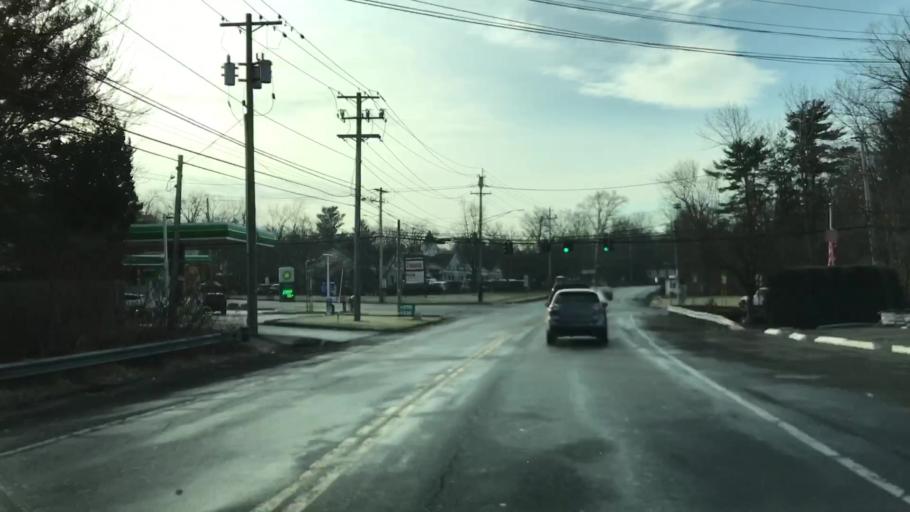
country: US
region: New York
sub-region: Rockland County
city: Congers
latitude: 41.1476
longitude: -73.9344
